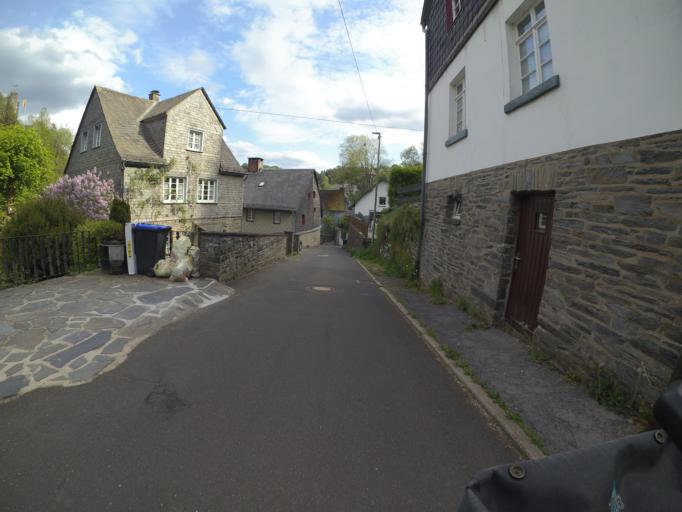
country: DE
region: North Rhine-Westphalia
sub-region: Regierungsbezirk Koln
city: Monschau
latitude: 50.5568
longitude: 6.2394
